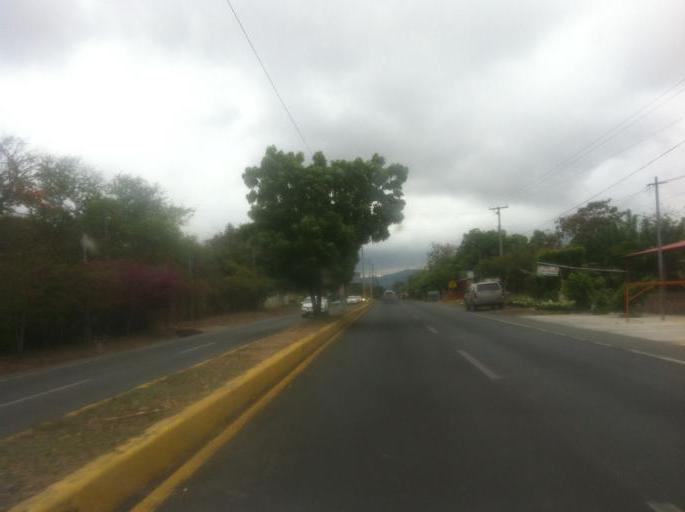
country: NI
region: Masaya
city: Ticuantepe
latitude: 12.0244
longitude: -86.1628
